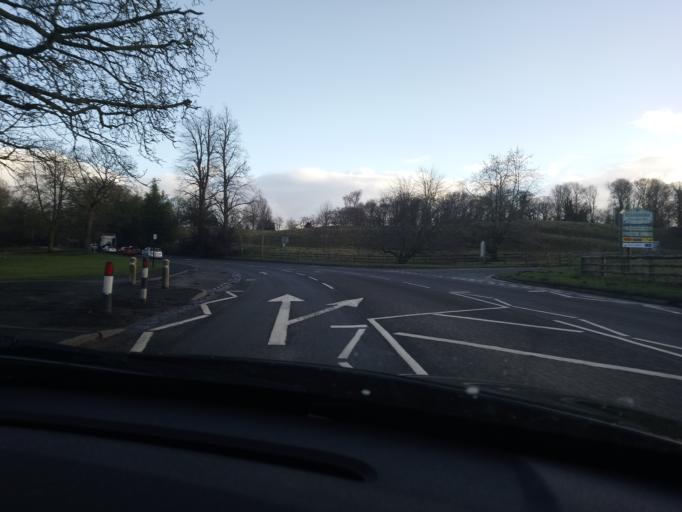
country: GB
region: England
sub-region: Shropshire
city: Ellesmere
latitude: 52.9056
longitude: -2.8849
